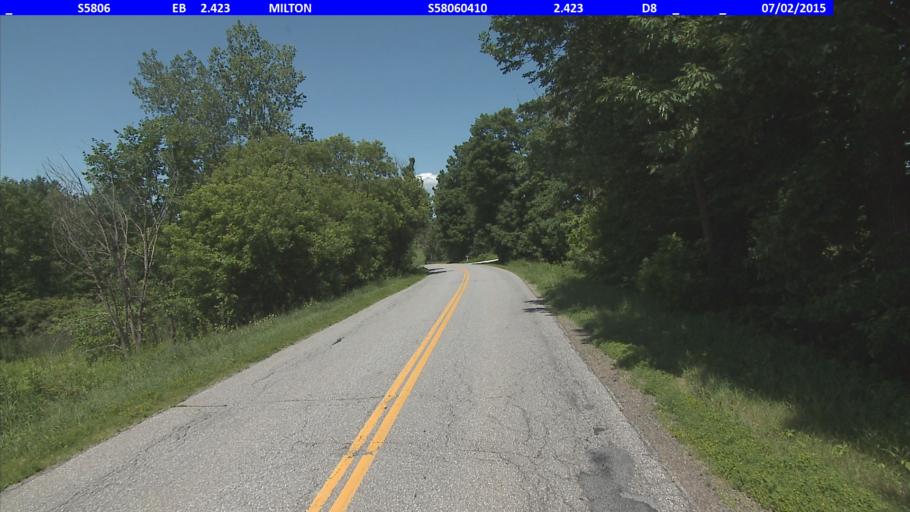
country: US
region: Vermont
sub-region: Chittenden County
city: Milton
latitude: 44.6652
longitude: -73.1566
